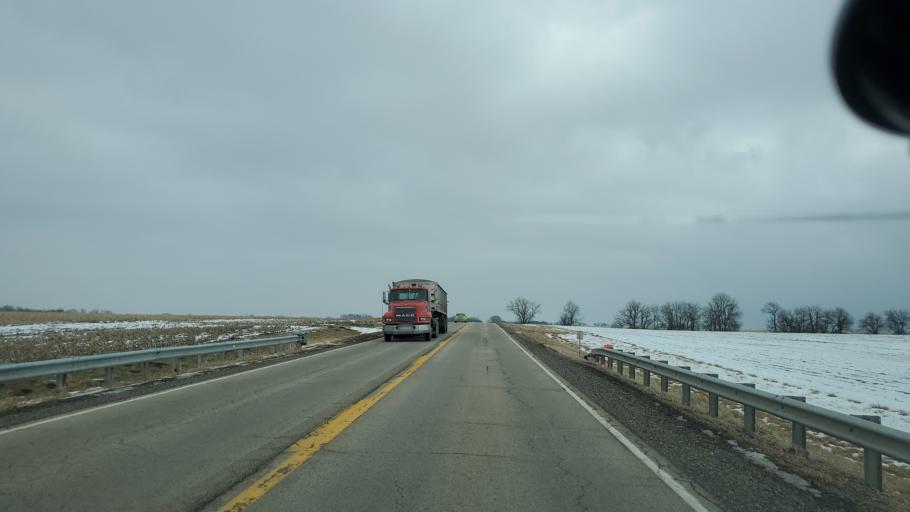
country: US
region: Illinois
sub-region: Marshall County
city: Toluca
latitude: 41.1186
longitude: -89.1752
